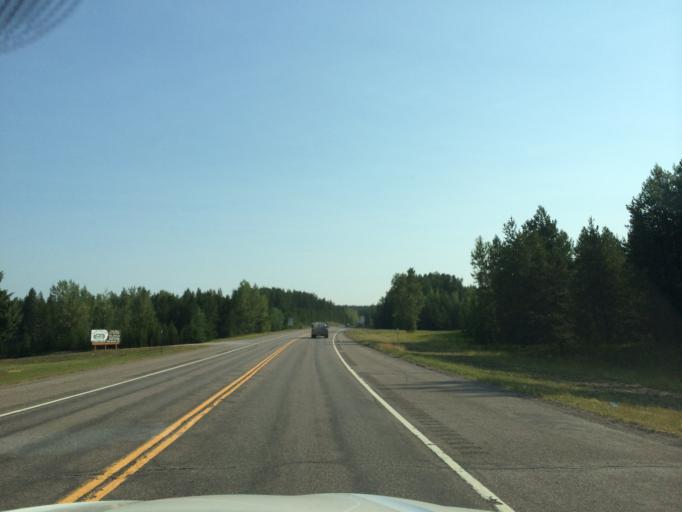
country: US
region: Montana
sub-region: Flathead County
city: Columbia Falls
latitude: 48.4401
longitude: -114.0406
